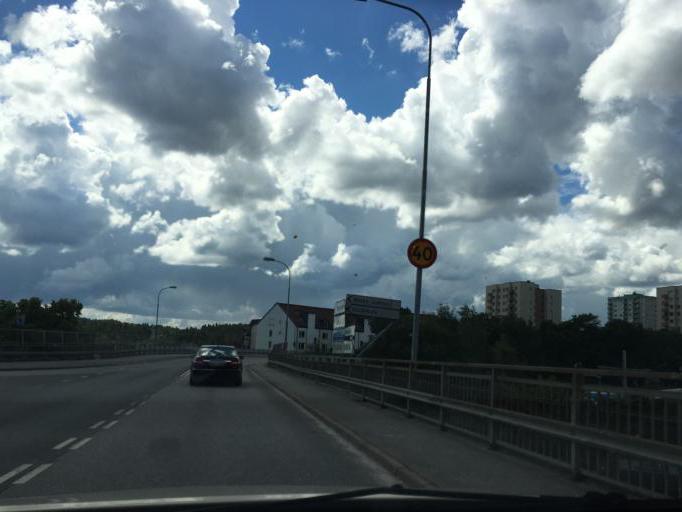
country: SE
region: Stockholm
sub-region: Nacka Kommun
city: Nacka
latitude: 59.3073
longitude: 18.1513
